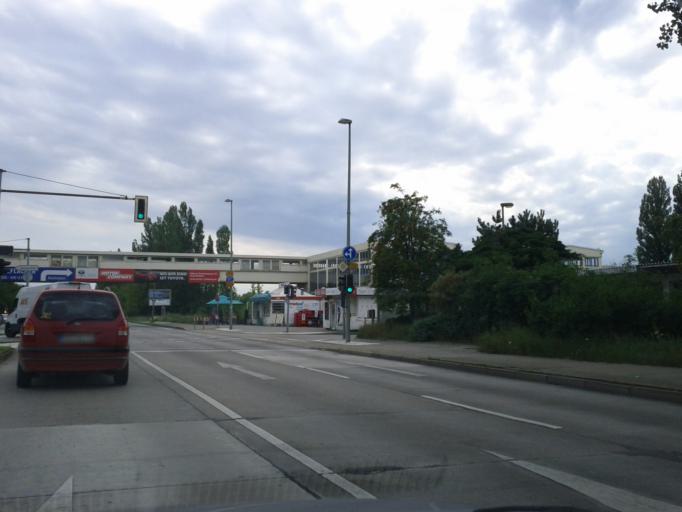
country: DE
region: Brandenburg
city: Ahrensfelde
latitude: 52.5708
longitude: 13.5658
